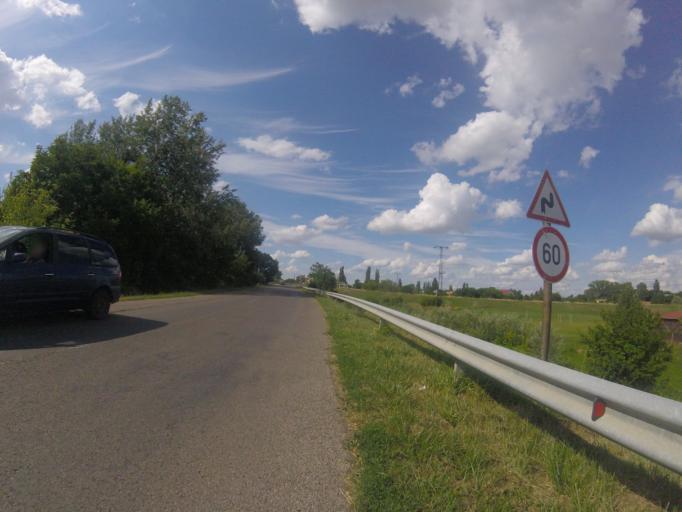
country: HU
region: Tolna
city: Szekszard
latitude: 46.3776
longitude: 18.7210
